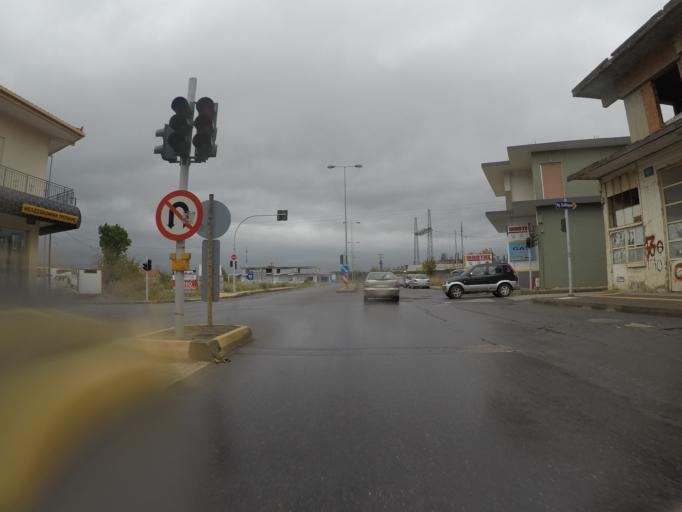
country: GR
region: Peloponnese
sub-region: Nomos Arkadias
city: Tripoli
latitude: 37.5029
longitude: 22.3771
